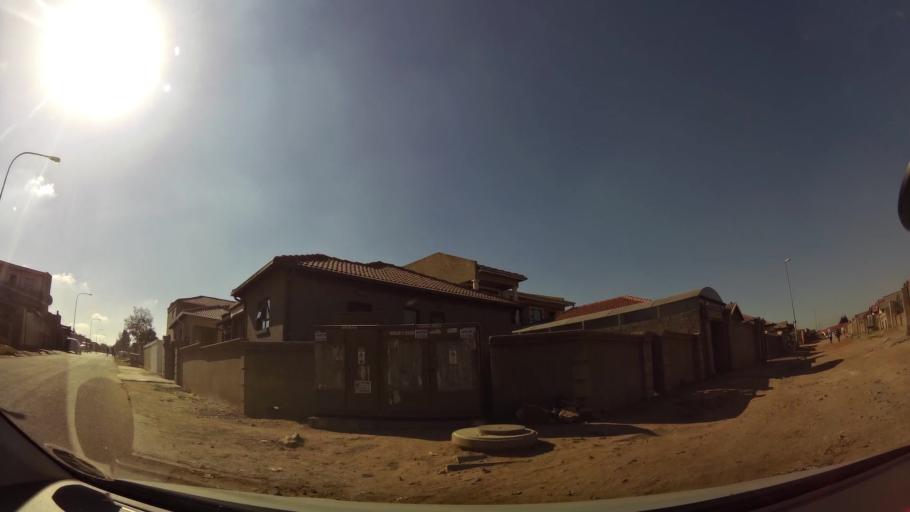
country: ZA
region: Gauteng
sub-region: City of Johannesburg Metropolitan Municipality
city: Roodepoort
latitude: -26.2176
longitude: 27.8872
